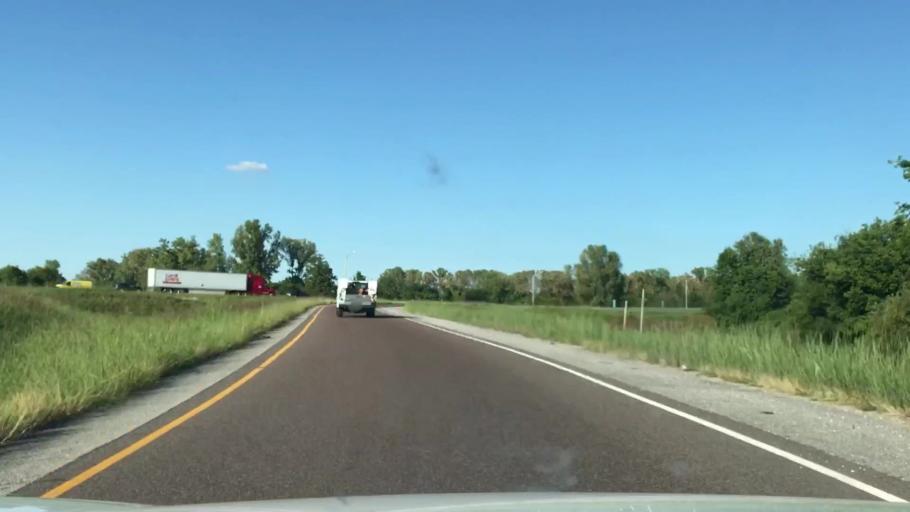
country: US
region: Illinois
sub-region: Madison County
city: Mitchell
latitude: 38.7649
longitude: -90.1218
